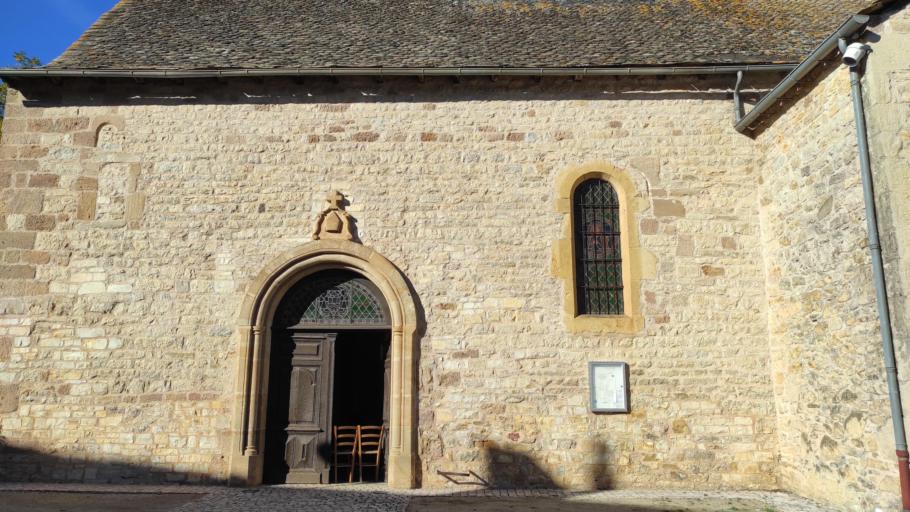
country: FR
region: Midi-Pyrenees
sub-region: Departement de l'Aveyron
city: Montbazens
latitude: 44.4229
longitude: 2.2177
